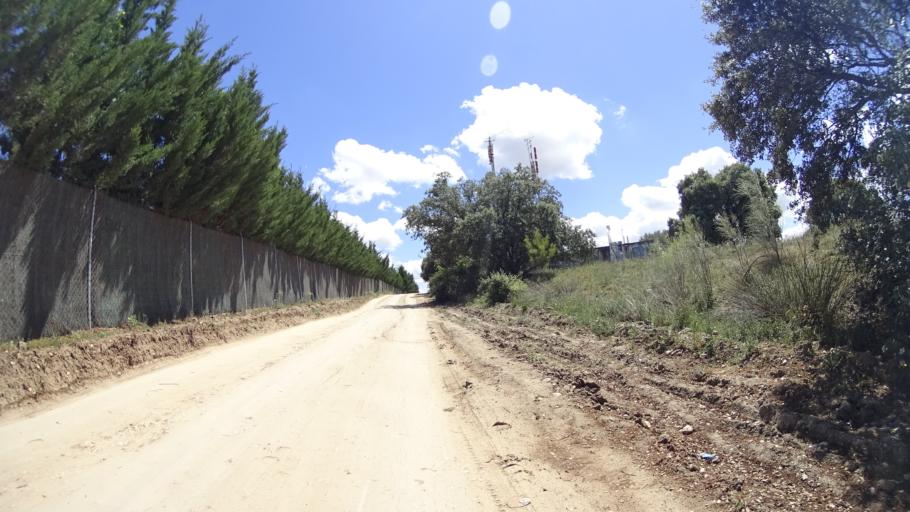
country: ES
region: Madrid
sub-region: Provincia de Madrid
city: Villanueva del Pardillo
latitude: 40.4670
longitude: -3.9616
